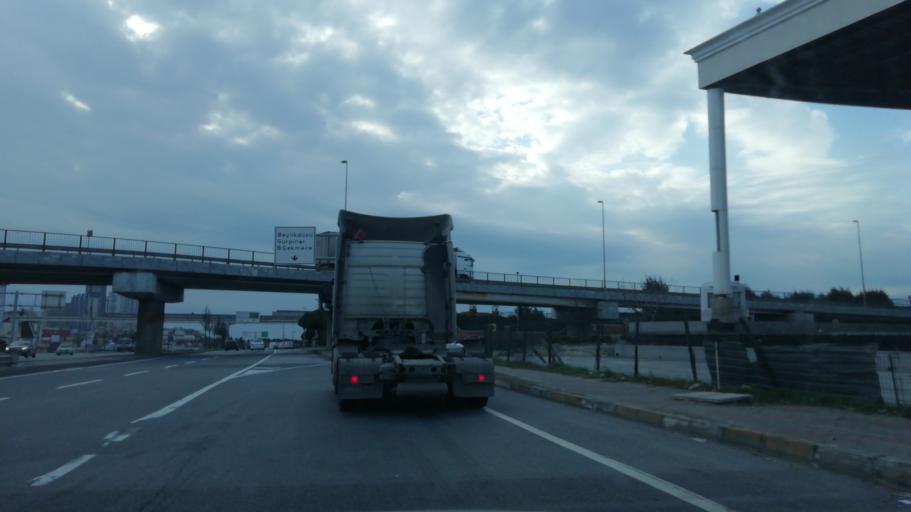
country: TR
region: Istanbul
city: Esenyurt
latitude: 41.0844
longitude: 28.6297
